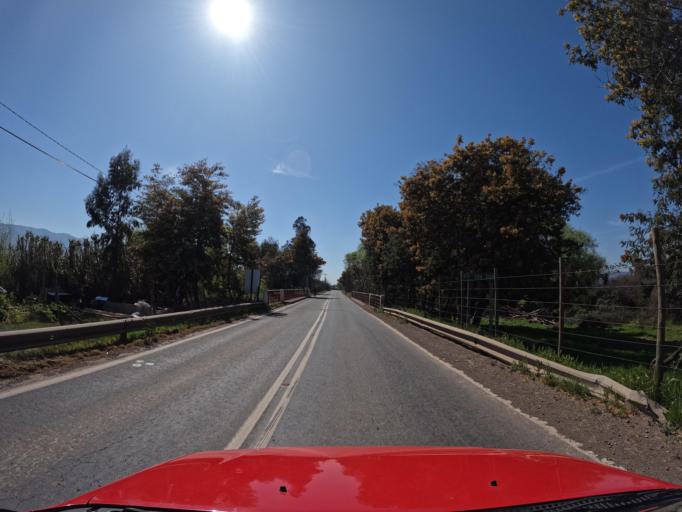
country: CL
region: Maule
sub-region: Provincia de Curico
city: Rauco
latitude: -35.0483
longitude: -71.4671
